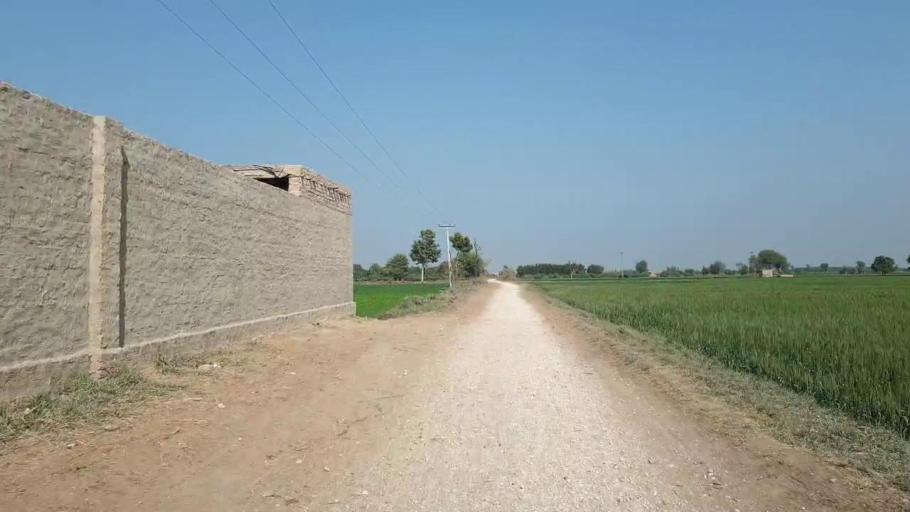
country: PK
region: Sindh
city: Hala
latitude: 25.9111
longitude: 68.4297
